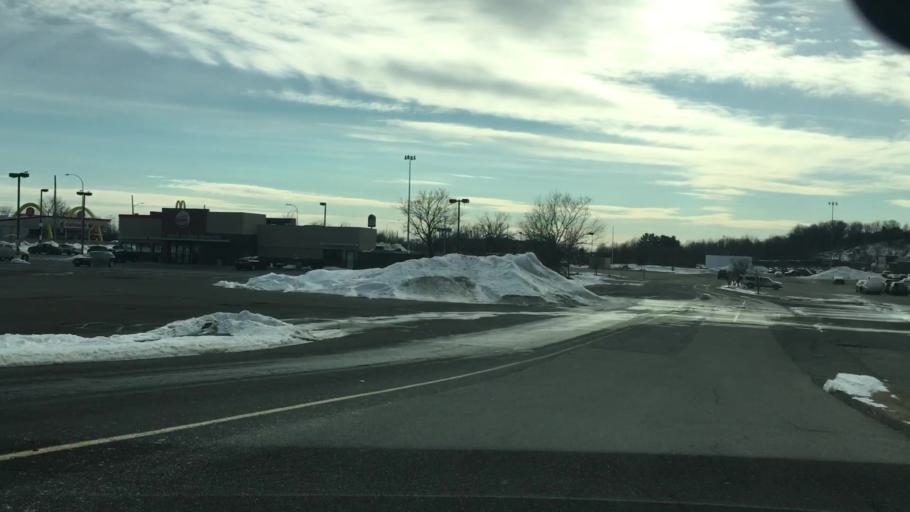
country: US
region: Massachusetts
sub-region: Hampden County
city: Holyoke
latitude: 42.1882
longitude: -72.6312
